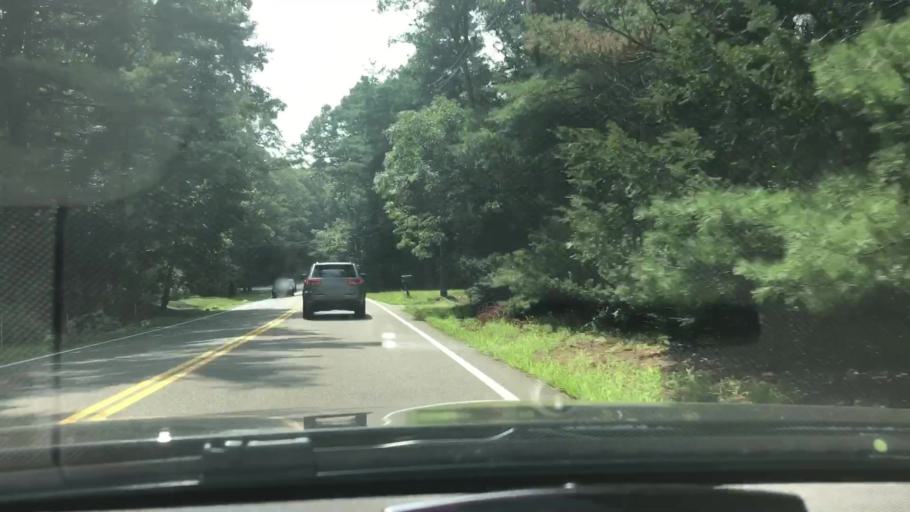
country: US
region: Massachusetts
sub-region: Norfolk County
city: Westwood
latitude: 42.2124
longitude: -71.2538
